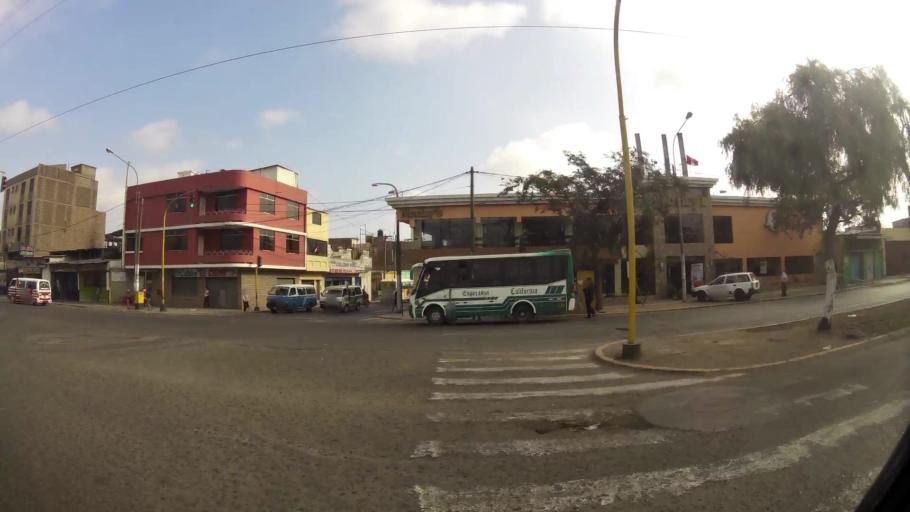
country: PE
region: La Libertad
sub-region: Provincia de Trujillo
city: El Porvenir
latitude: -8.1000
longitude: -79.0129
